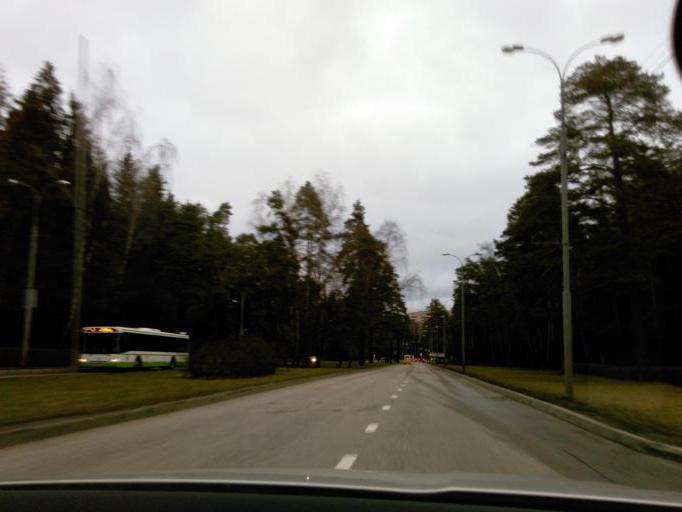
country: RU
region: Moskovskaya
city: Rzhavki
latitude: 55.9934
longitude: 37.2282
